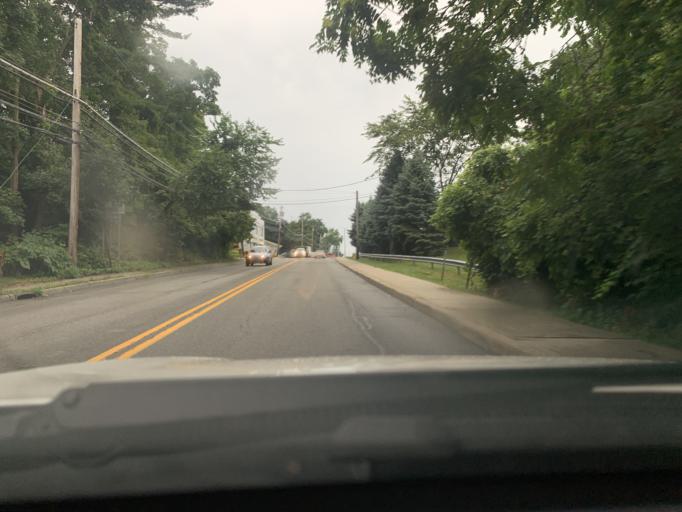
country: US
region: New York
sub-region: Westchester County
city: Ossining
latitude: 41.1762
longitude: -73.8680
